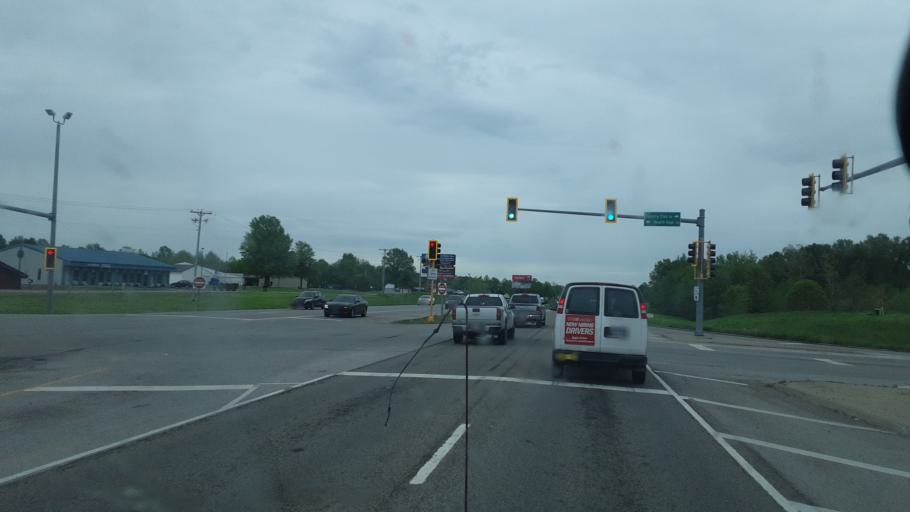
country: US
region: Illinois
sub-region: Jackson County
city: Murphysboro
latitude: 37.7616
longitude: -89.2809
